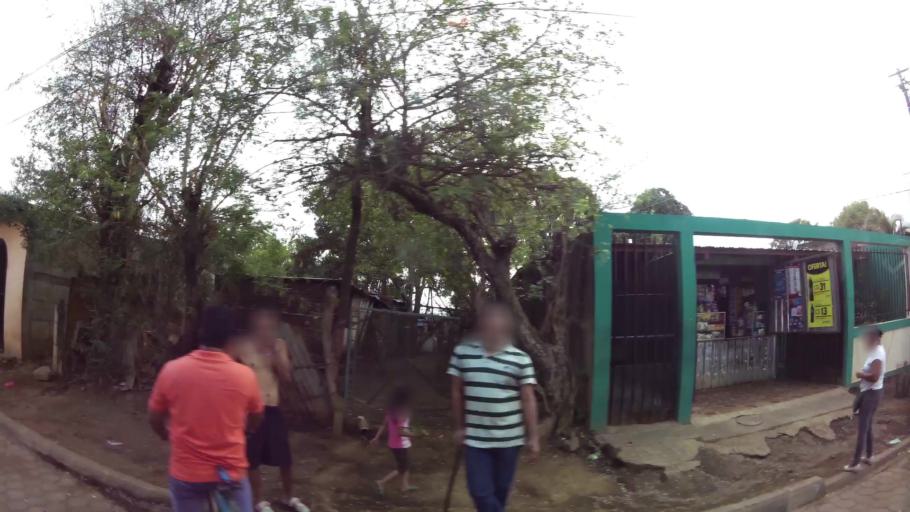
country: NI
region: Masaya
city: Masaya
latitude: 11.9851
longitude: -86.1054
